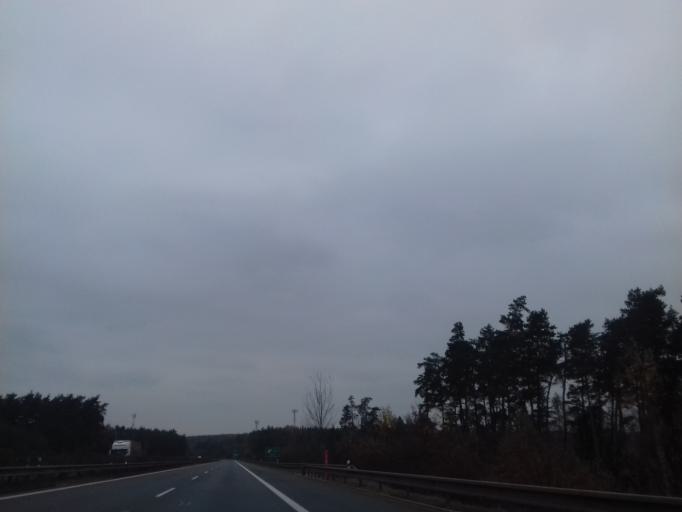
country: CZ
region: Plzensky
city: Vejprnice
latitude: 49.6995
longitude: 13.2917
